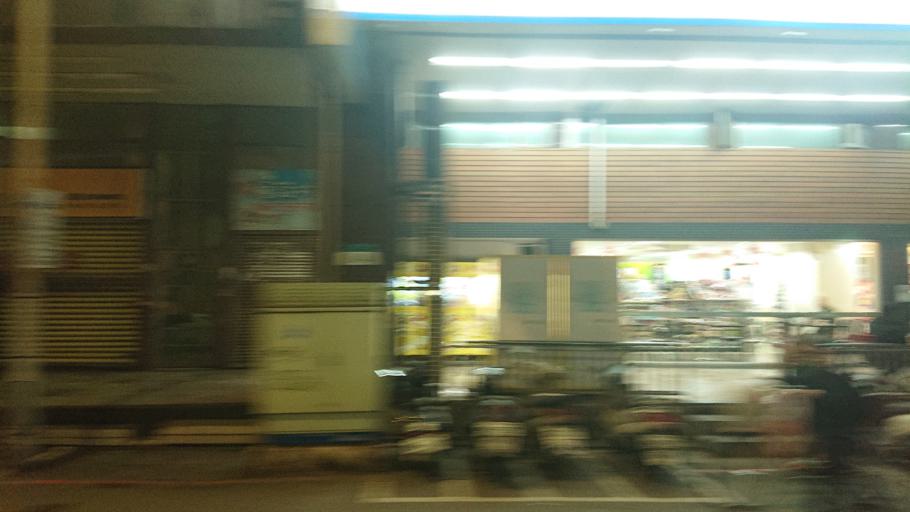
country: TW
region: Taiwan
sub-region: Taoyuan
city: Taoyuan
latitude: 24.9279
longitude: 121.3759
